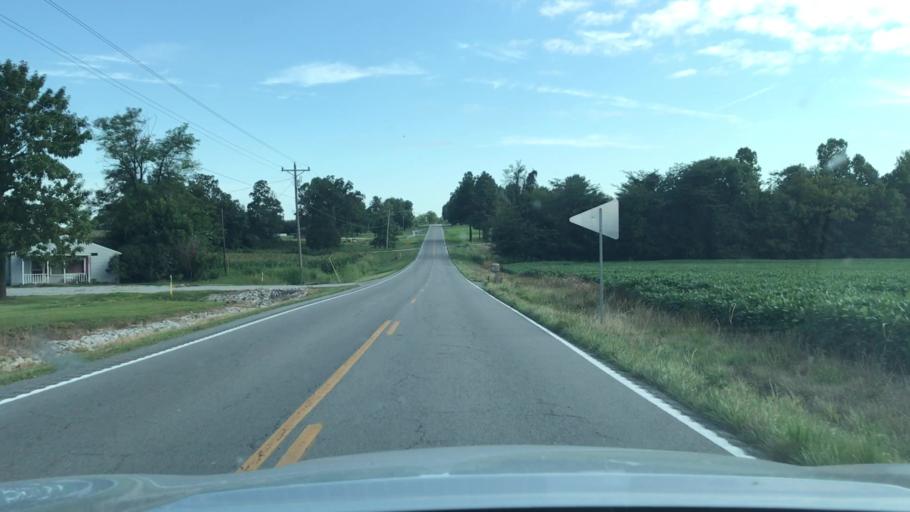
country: US
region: Kentucky
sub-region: Todd County
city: Elkton
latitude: 36.8794
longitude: -87.1671
